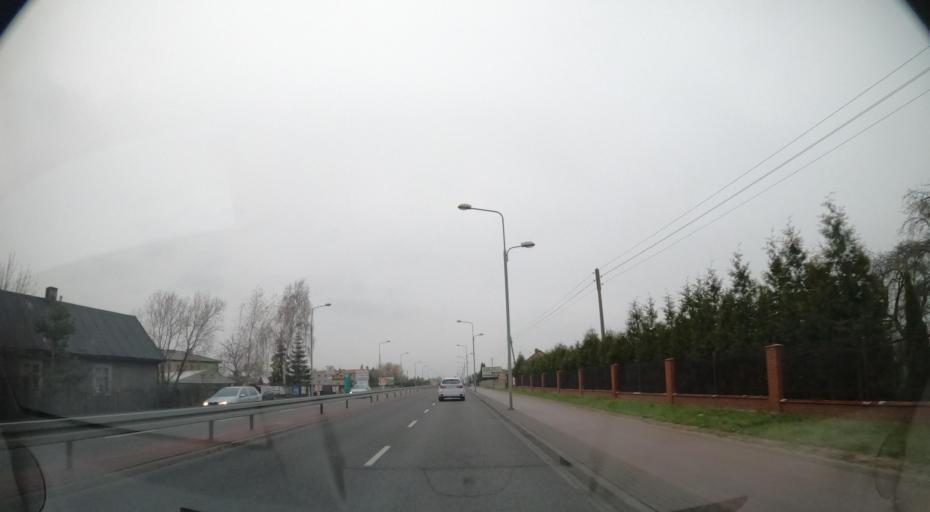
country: PL
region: Masovian Voivodeship
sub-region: Radom
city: Radom
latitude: 51.4224
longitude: 21.2155
